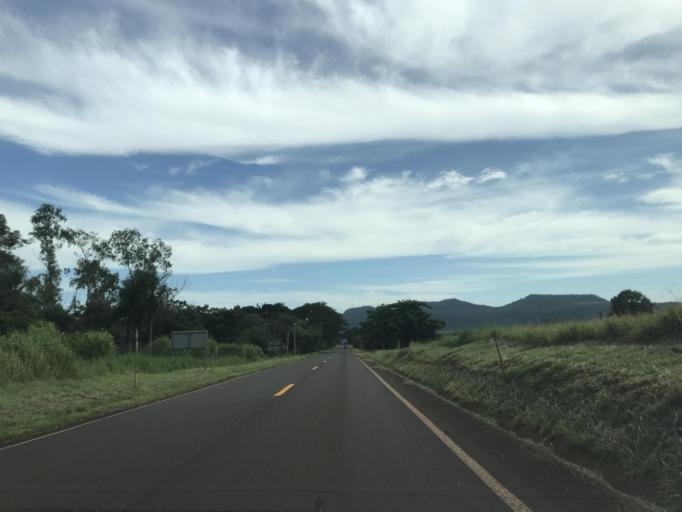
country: BR
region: Parana
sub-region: Paranavai
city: Nova Aurora
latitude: -22.8185
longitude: -52.6549
